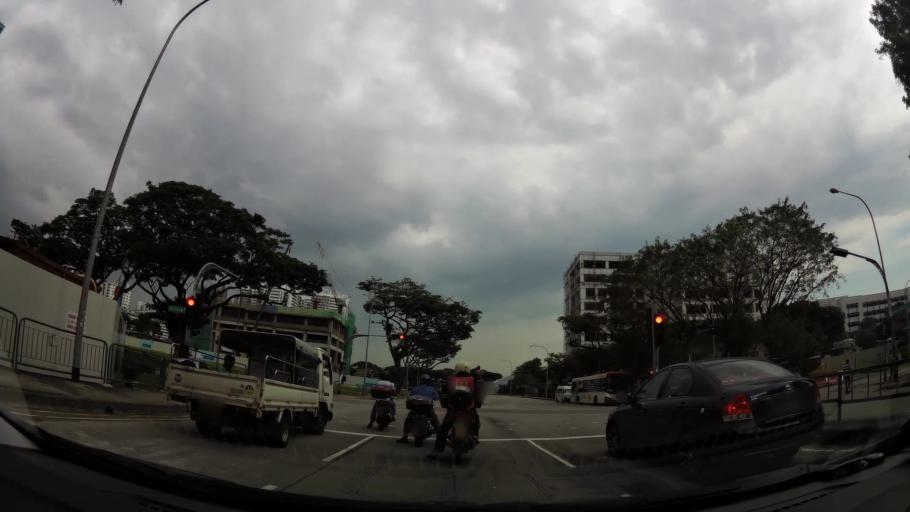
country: SG
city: Singapore
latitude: 1.3141
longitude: 103.8661
